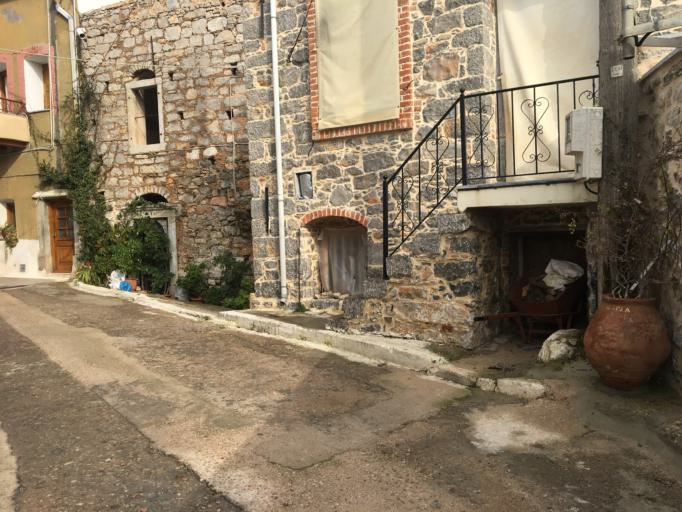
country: GR
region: North Aegean
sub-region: Chios
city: Thymiana
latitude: 38.2467
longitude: 25.9435
